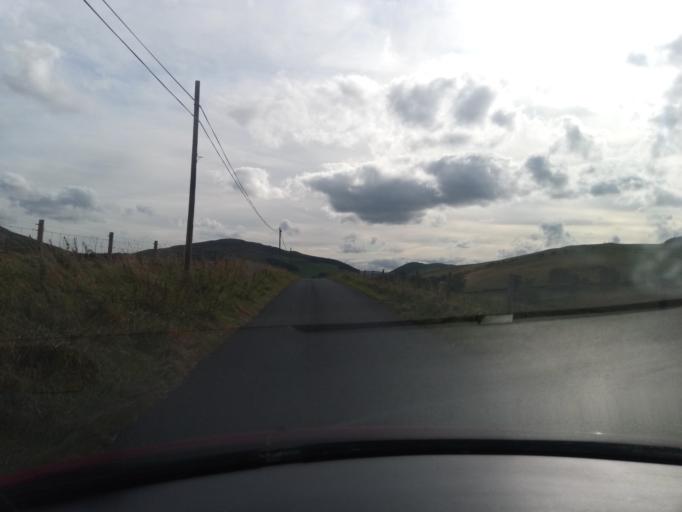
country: GB
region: Scotland
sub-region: The Scottish Borders
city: Kelso
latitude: 55.4745
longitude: -2.3529
